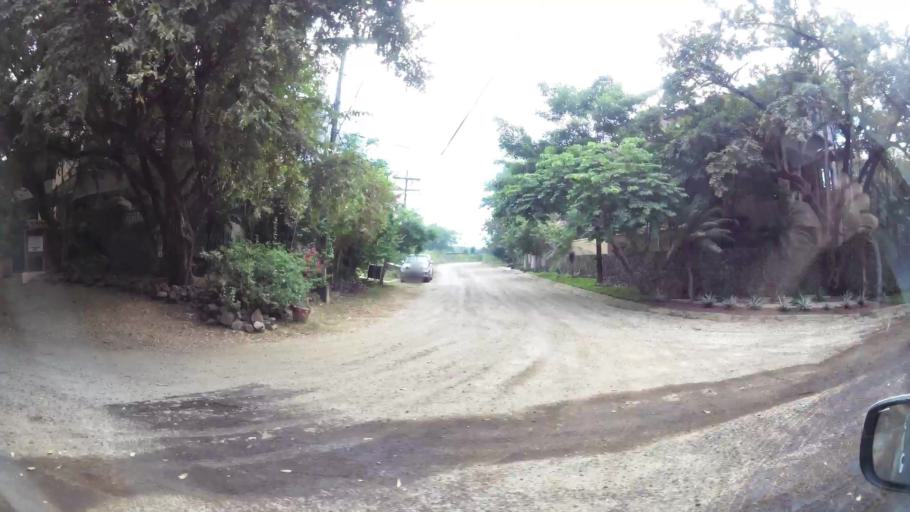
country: CR
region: Guanacaste
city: Santa Cruz
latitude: 10.2903
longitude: -85.8514
